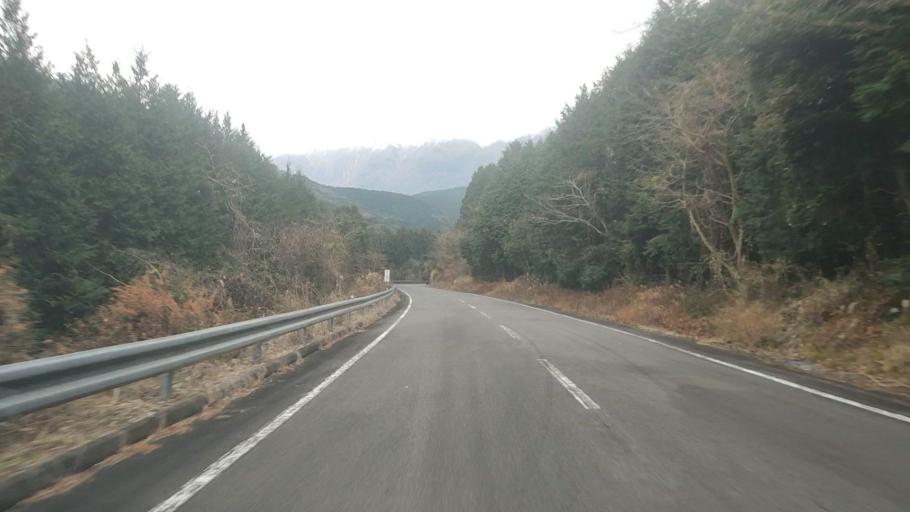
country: JP
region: Nagasaki
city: Shimabara
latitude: 32.7898
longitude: 130.2826
